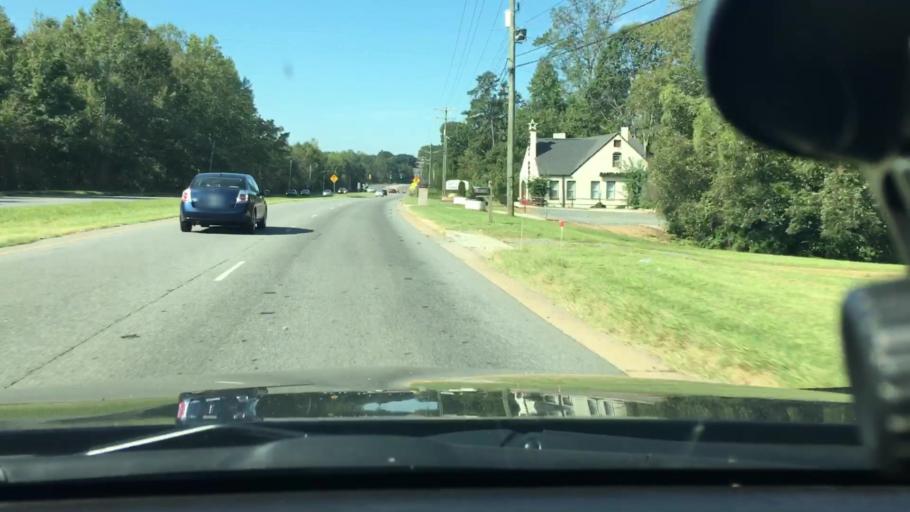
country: US
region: North Carolina
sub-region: Mecklenburg County
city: Mint Hill
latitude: 35.2246
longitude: -80.6174
